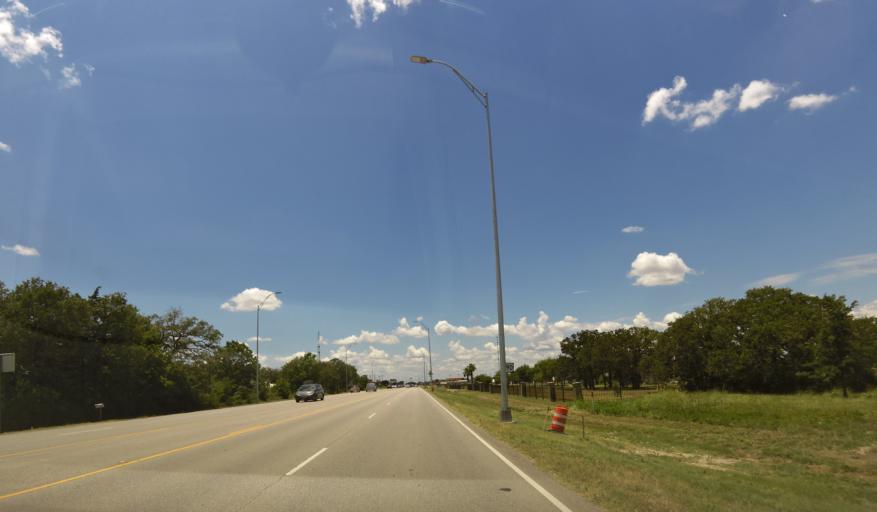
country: US
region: Texas
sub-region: Lee County
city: Giddings
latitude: 30.1772
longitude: -96.9014
